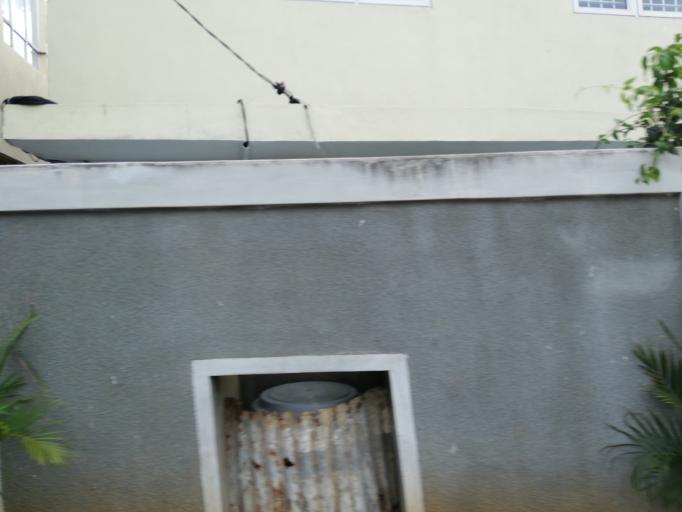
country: MU
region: Black River
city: Petite Riviere
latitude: -20.2155
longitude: 57.4659
